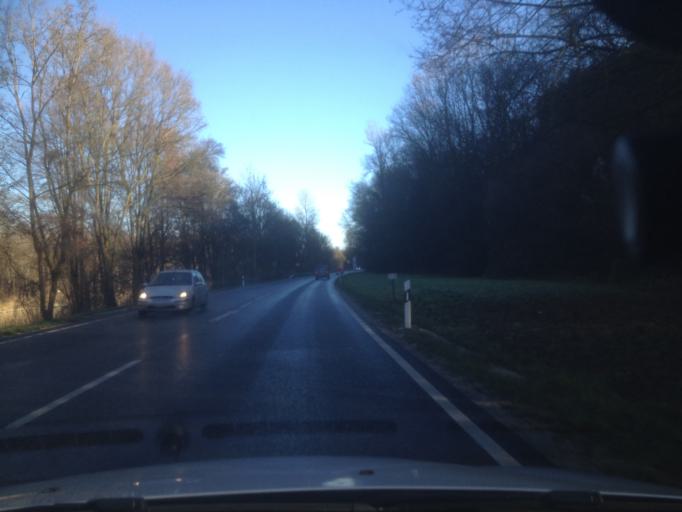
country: DE
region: Bavaria
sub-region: Lower Bavaria
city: Landshut
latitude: 48.5245
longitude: 12.1266
